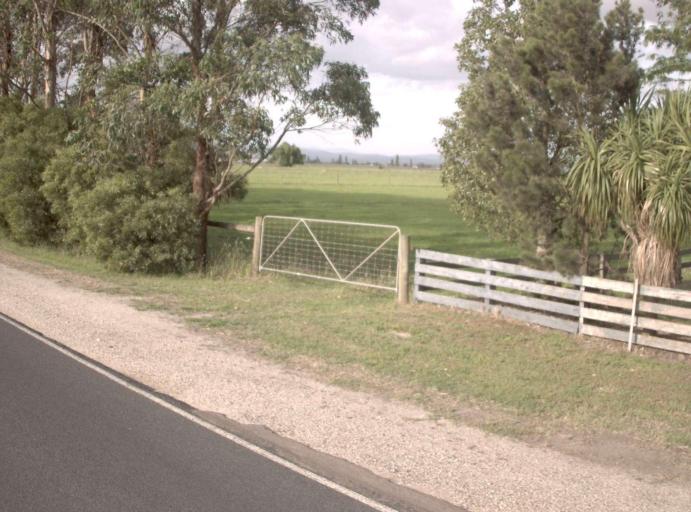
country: AU
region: Victoria
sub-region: Wellington
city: Sale
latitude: -37.9096
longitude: 146.9957
